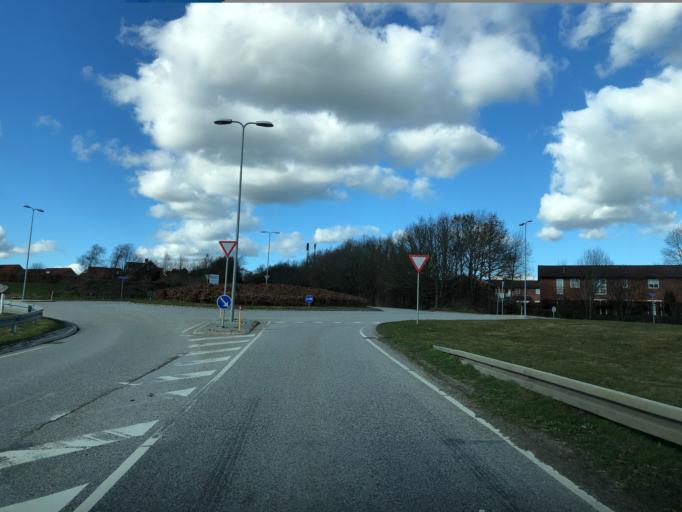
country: DK
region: Central Jutland
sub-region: Favrskov Kommune
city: Hinnerup
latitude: 56.2717
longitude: 10.0508
